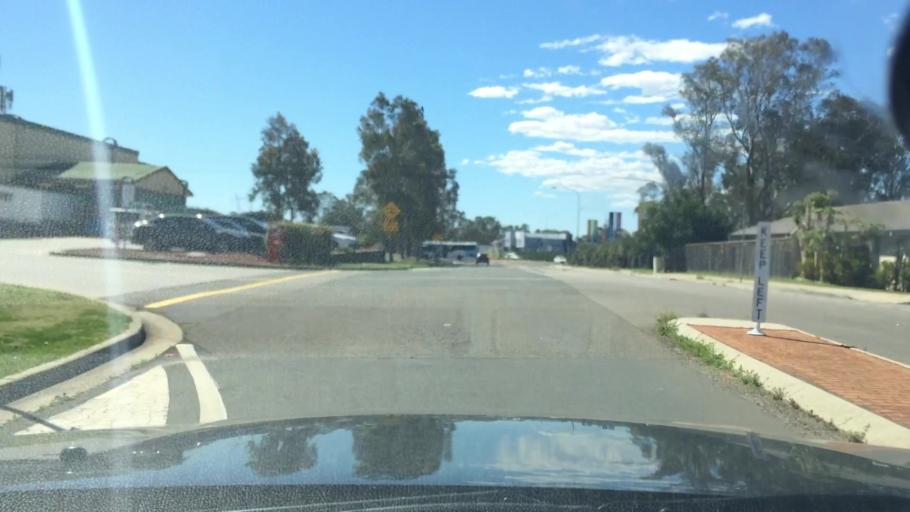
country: AU
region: New South Wales
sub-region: Liverpool
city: Miller
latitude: -33.9377
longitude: 150.8464
